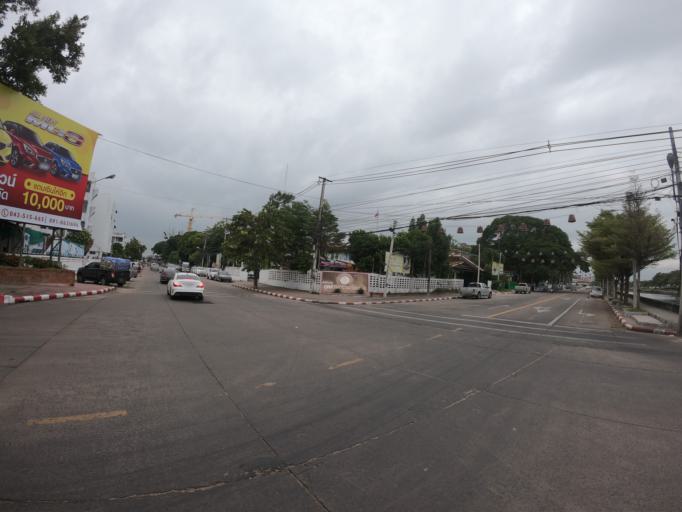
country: TH
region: Roi Et
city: Roi Et
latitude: 16.0496
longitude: 103.6514
